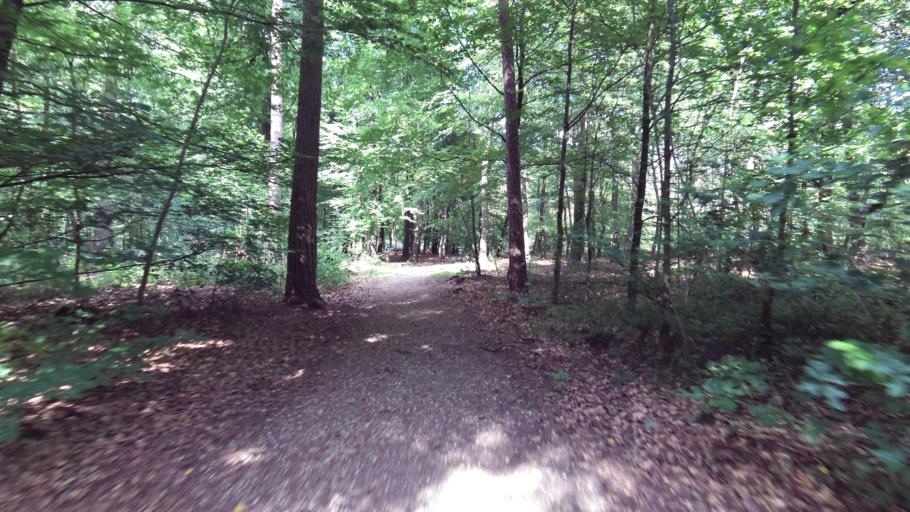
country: NL
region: Gelderland
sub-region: Gemeente Epe
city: Vaassen
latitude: 52.2781
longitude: 5.9211
